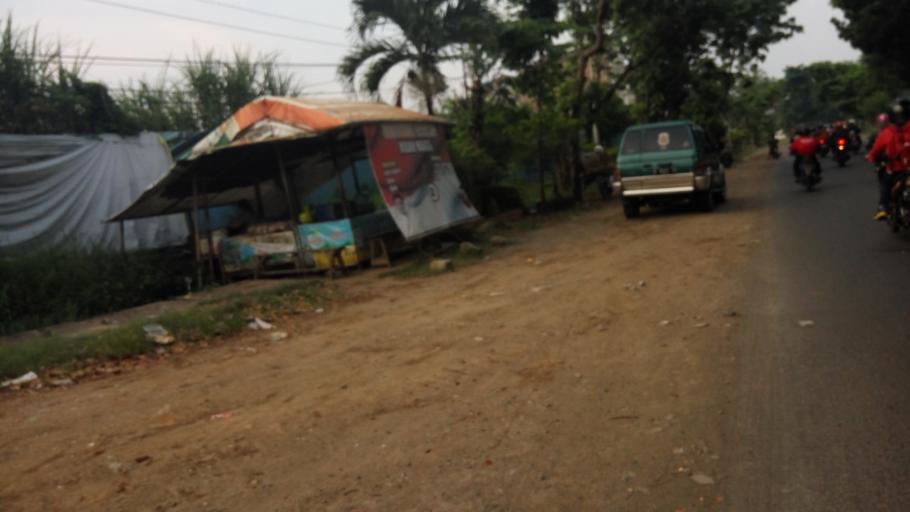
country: ID
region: Central Java
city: Semarang
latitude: -7.0078
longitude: 110.3877
